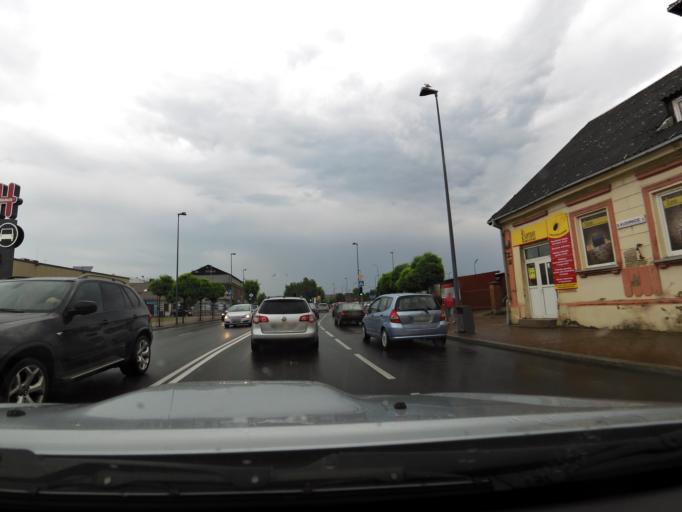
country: LT
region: Marijampoles apskritis
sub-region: Marijampole Municipality
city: Marijampole
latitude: 54.5558
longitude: 23.3543
